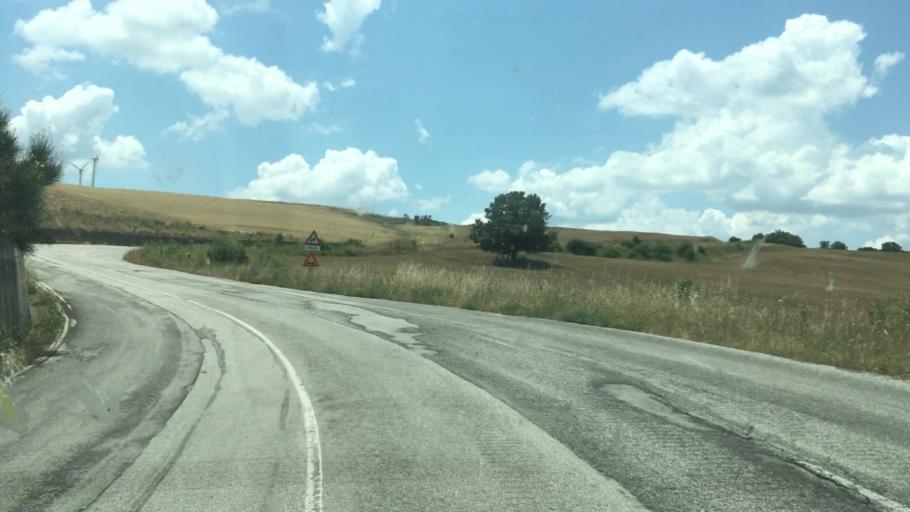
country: IT
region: Basilicate
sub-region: Provincia di Potenza
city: Tolve
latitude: 40.6860
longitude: 15.9792
